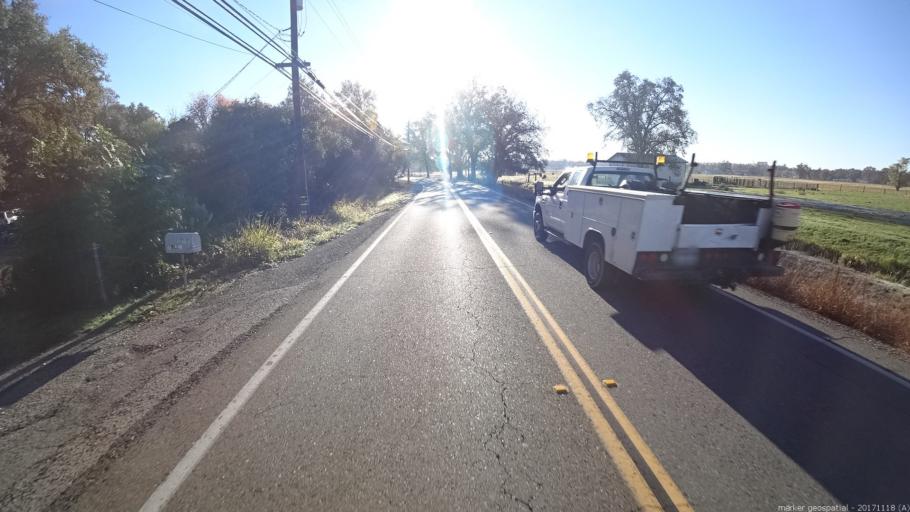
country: US
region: California
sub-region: Shasta County
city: Anderson
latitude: 40.4517
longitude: -122.2686
